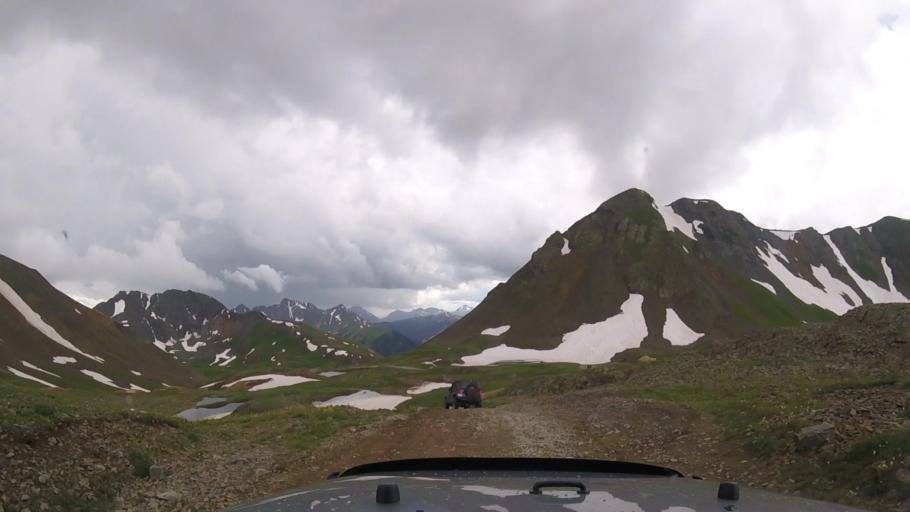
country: US
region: Colorado
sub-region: Ouray County
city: Ouray
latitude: 37.9198
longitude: -107.6275
